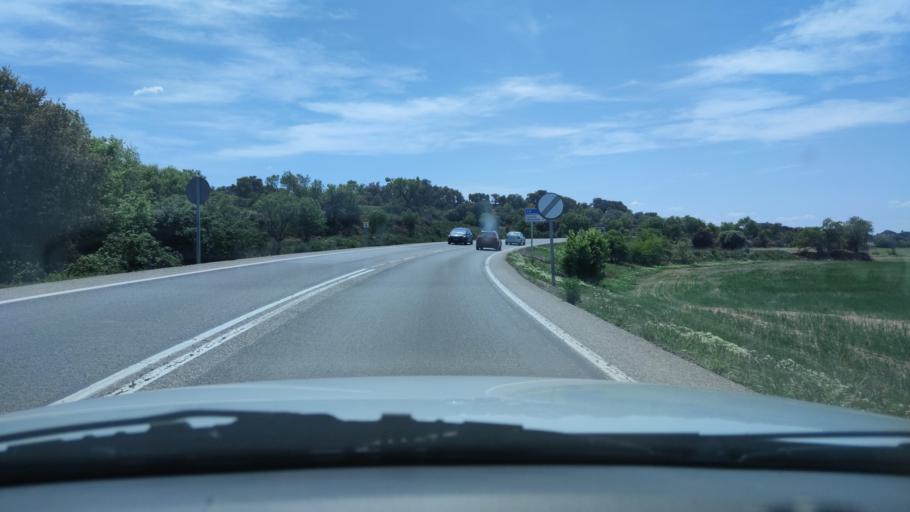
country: ES
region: Catalonia
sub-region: Provincia de Lleida
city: Tarrega
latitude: 41.6930
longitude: 1.1689
